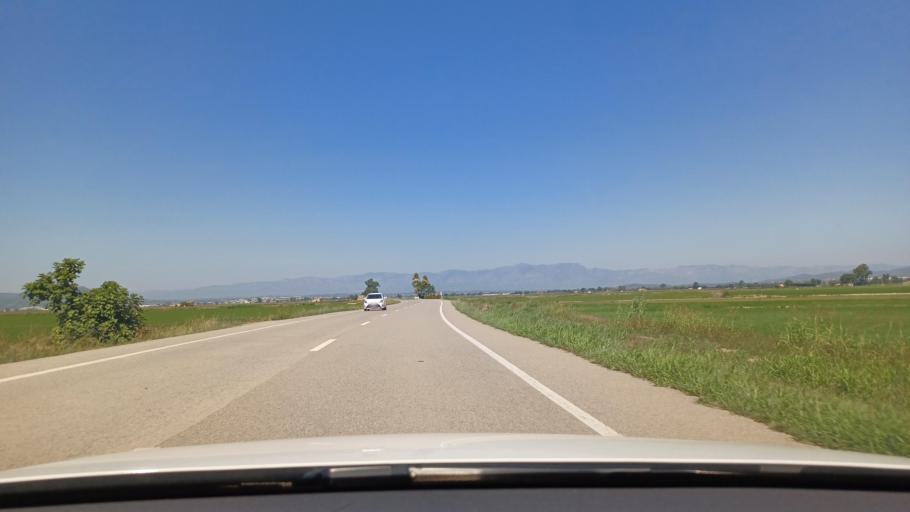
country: ES
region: Catalonia
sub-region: Provincia de Tarragona
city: Deltebre
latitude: 40.7024
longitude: 0.6676
